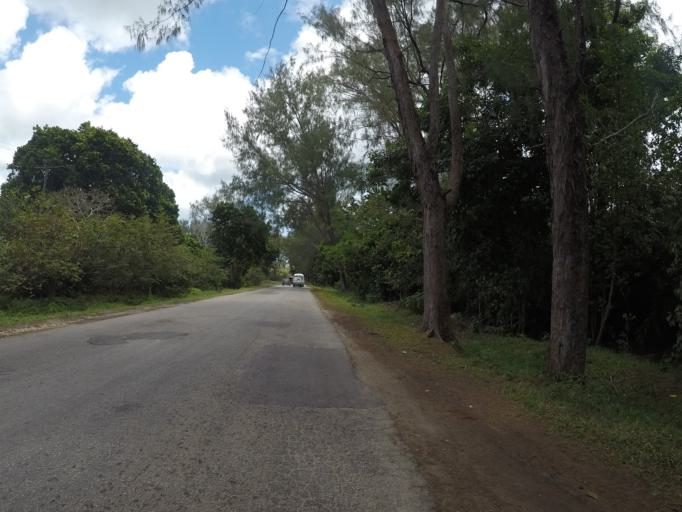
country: TZ
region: Zanzibar Central/South
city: Mahonda
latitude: -6.2757
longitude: 39.4165
